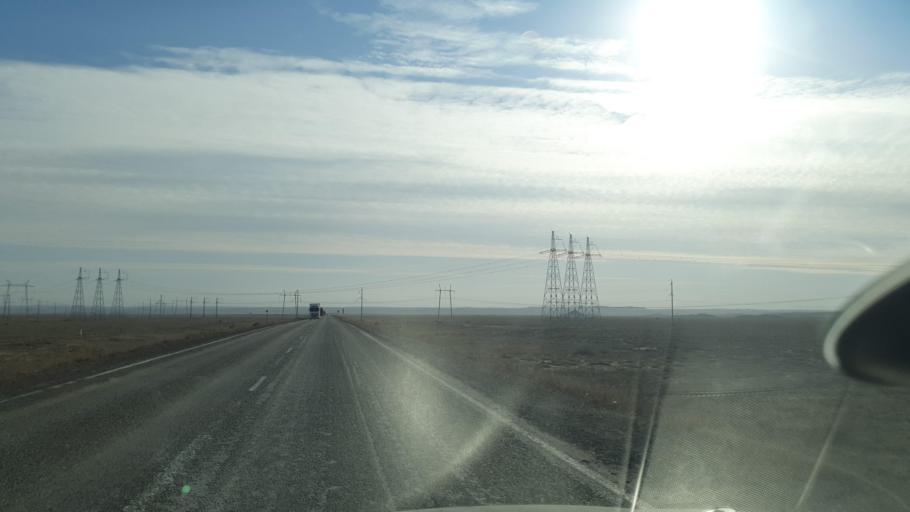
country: KZ
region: Zhambyl
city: Mynaral
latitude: 45.6029
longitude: 73.3984
